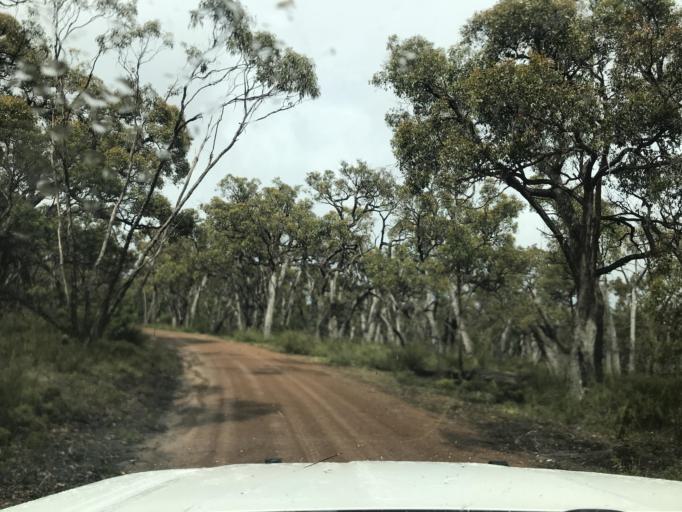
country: AU
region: South Australia
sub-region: Wattle Range
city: Penola
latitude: -37.2605
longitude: 141.3297
